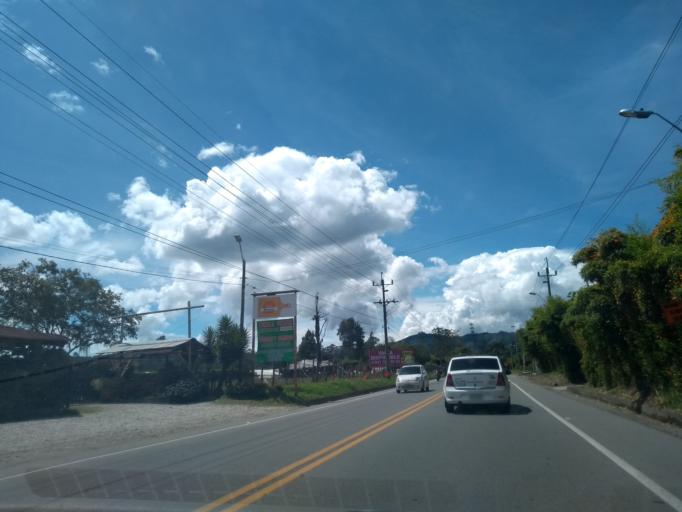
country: CO
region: Antioquia
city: La Ceja
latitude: 6.0420
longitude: -75.4027
